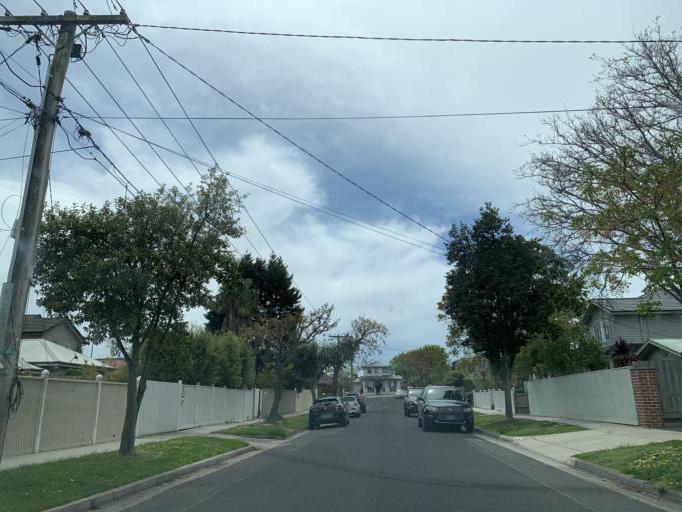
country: AU
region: Victoria
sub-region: Bayside
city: Hampton East
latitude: -37.9482
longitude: 145.0281
